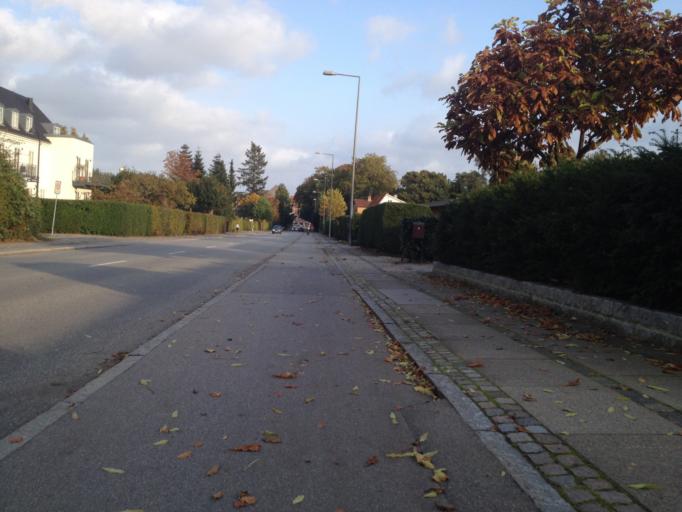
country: DK
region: Capital Region
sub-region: Gentofte Kommune
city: Charlottenlund
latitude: 55.7402
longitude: 12.5694
